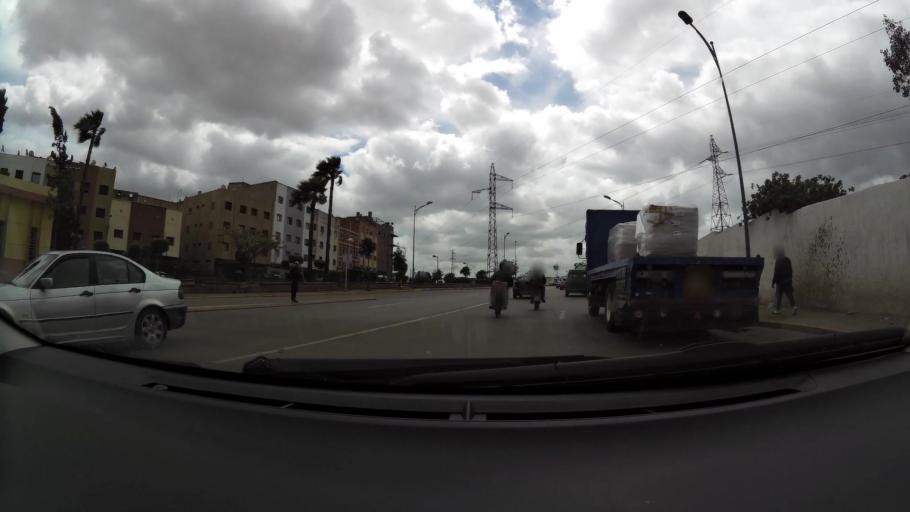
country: MA
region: Grand Casablanca
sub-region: Casablanca
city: Casablanca
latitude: 33.5866
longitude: -7.5460
